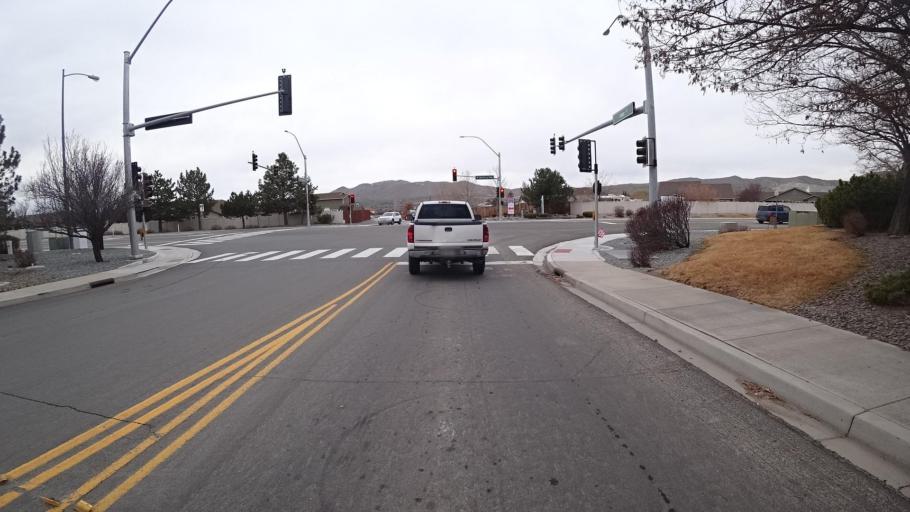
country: US
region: Nevada
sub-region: Washoe County
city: Spanish Springs
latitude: 39.6691
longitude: -119.7068
